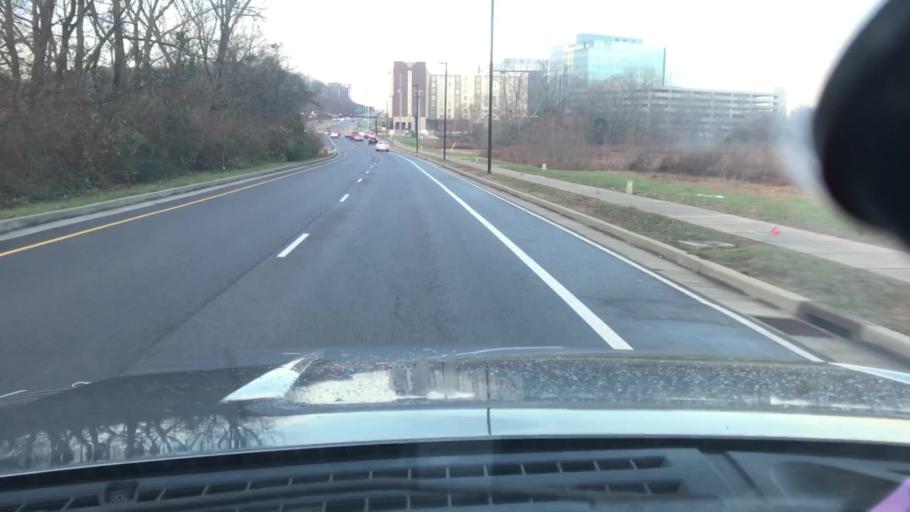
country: US
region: Tennessee
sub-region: Williamson County
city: Franklin
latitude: 35.9329
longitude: -86.8087
